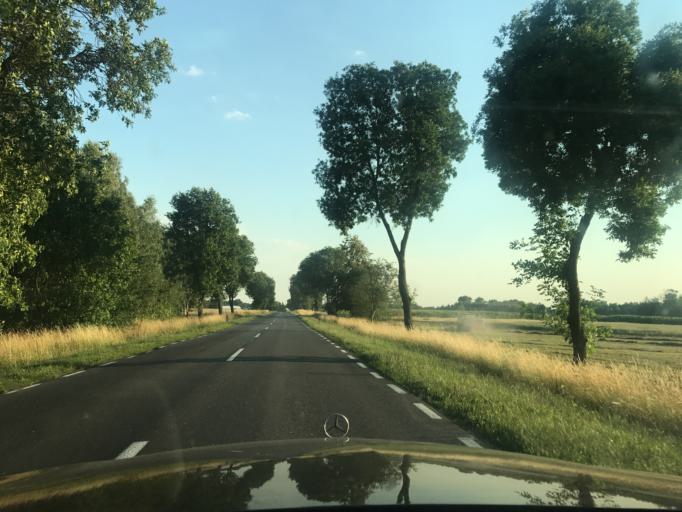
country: PL
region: Lublin Voivodeship
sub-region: Powiat parczewski
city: Debowa Kloda
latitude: 51.6597
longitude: 23.0043
